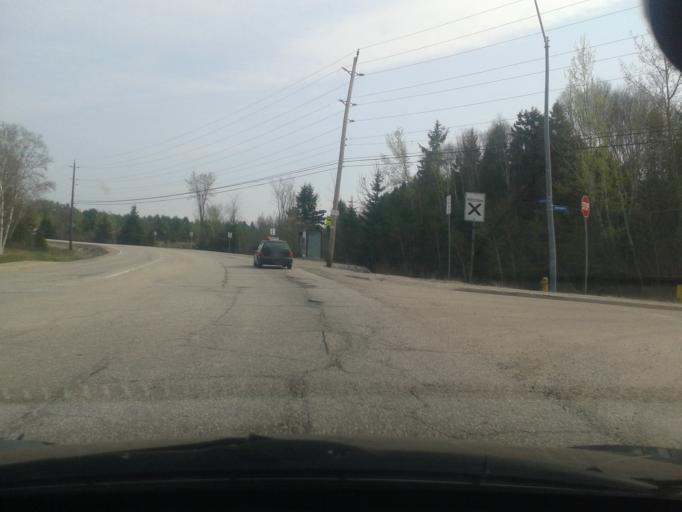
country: CA
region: Ontario
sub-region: Nipissing District
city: North Bay
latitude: 46.3419
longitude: -79.4875
